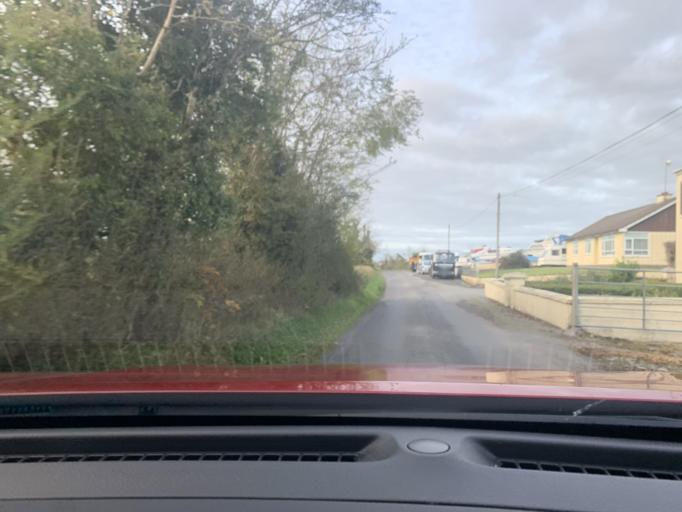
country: IE
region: Connaught
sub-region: Roscommon
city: Ballaghaderreen
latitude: 53.9990
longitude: -8.6068
